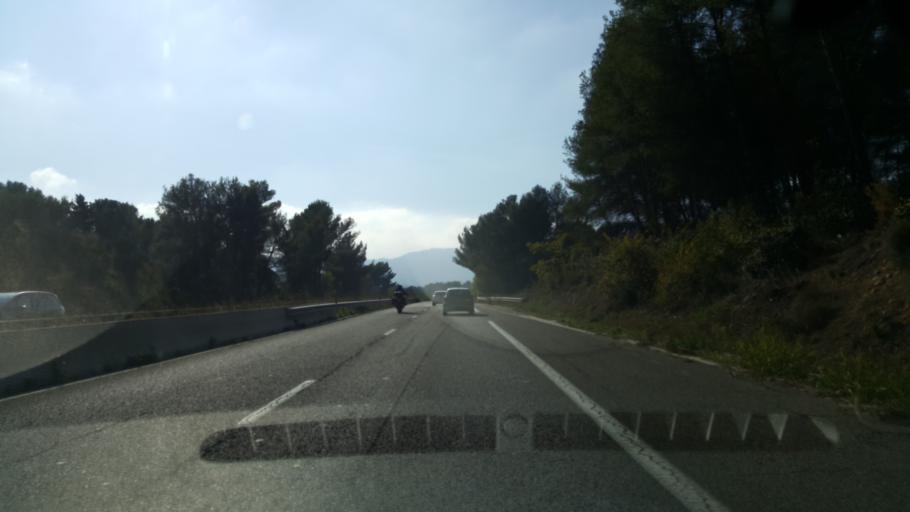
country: FR
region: Provence-Alpes-Cote d'Azur
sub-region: Departement des Bouches-du-Rhone
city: Aubagne
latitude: 43.2996
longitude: 5.5637
